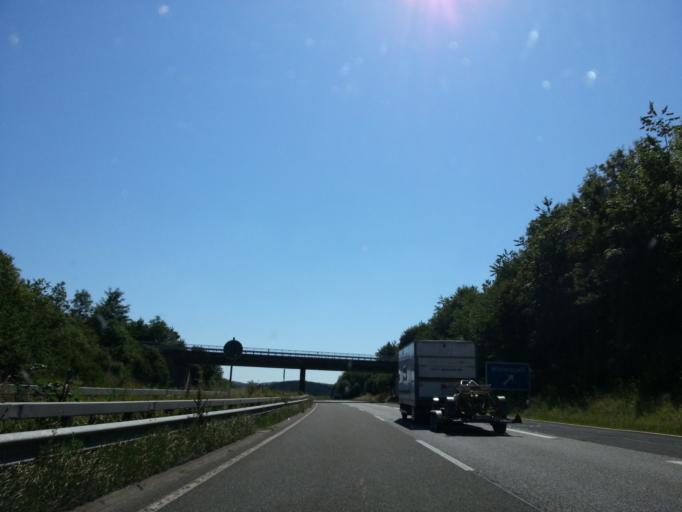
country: DE
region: Rheinland-Pfalz
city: Winterspelt
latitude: 50.2272
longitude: 6.1916
